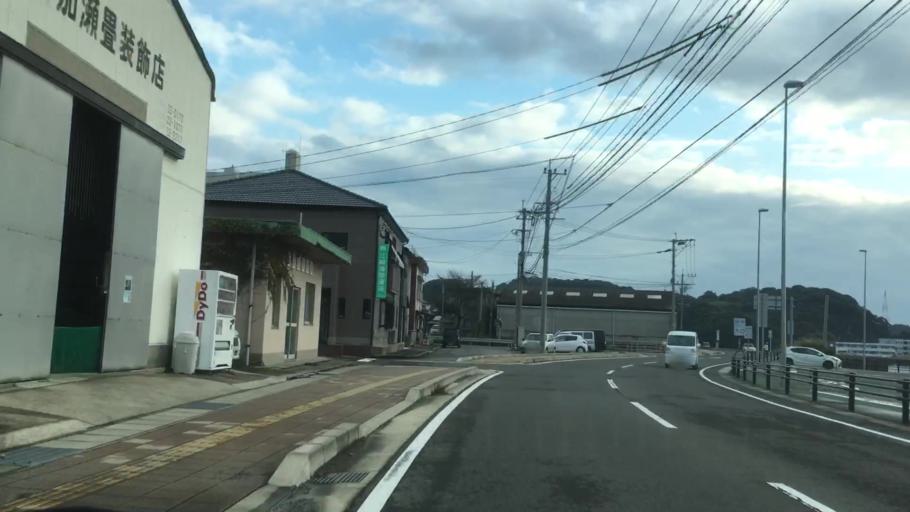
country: JP
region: Nagasaki
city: Sasebo
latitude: 32.9400
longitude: 129.6392
